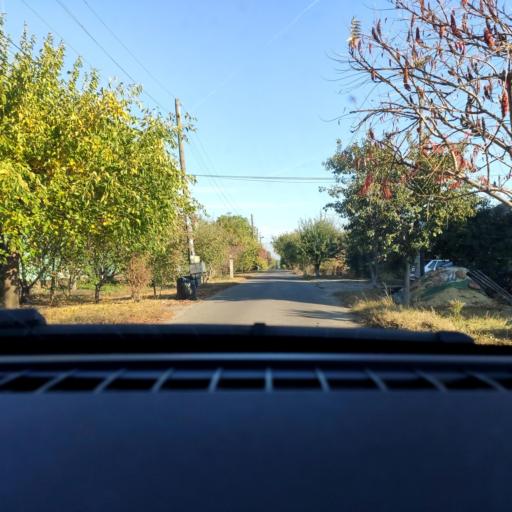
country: RU
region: Voronezj
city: Voronezh
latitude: 51.6633
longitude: 39.2630
